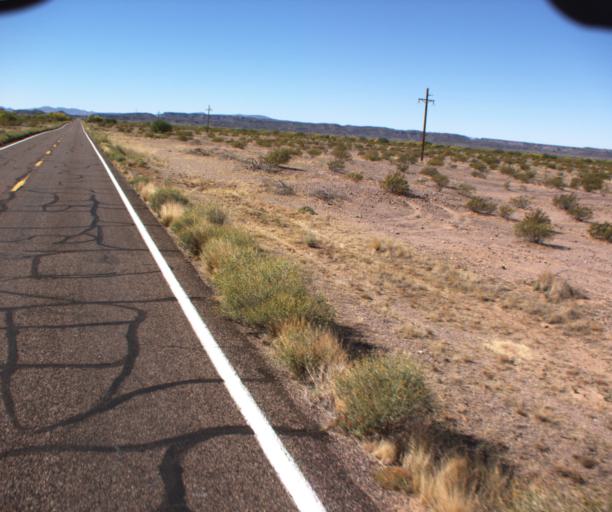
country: US
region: Arizona
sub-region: Pima County
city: Ajo
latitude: 32.6214
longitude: -112.8666
